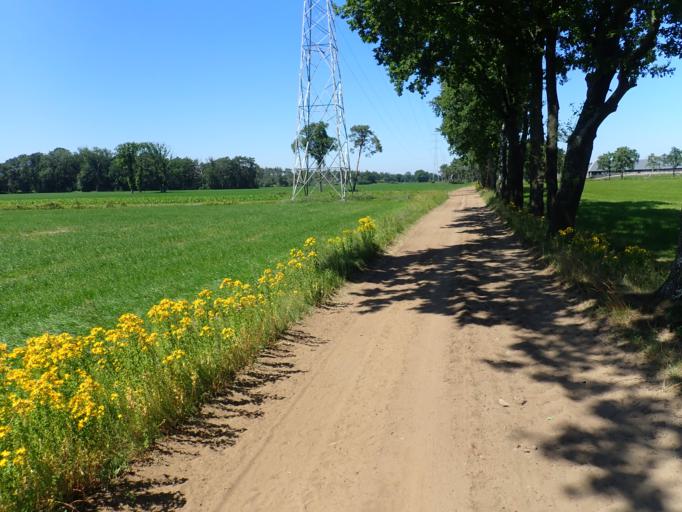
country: BE
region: Flanders
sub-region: Provincie Antwerpen
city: Beerse
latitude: 51.2874
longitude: 4.8335
